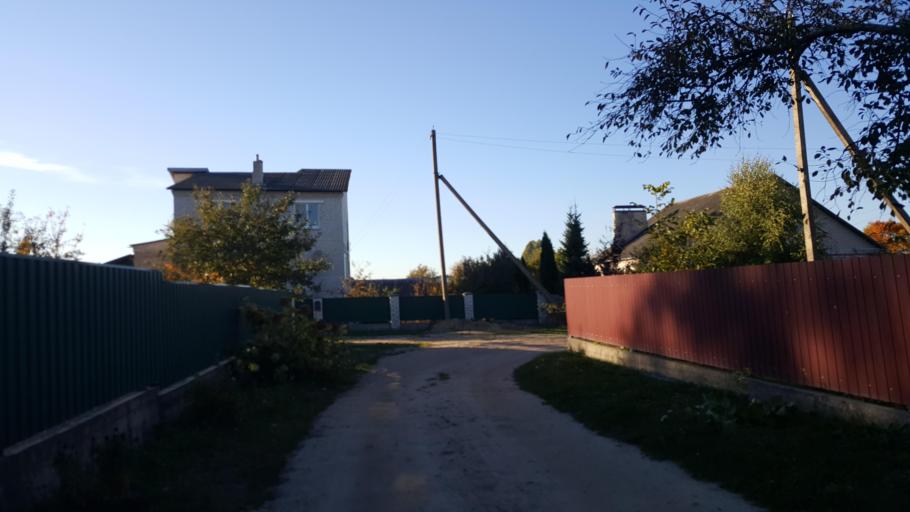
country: BY
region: Brest
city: Kamyanyets
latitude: 52.4000
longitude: 23.8352
